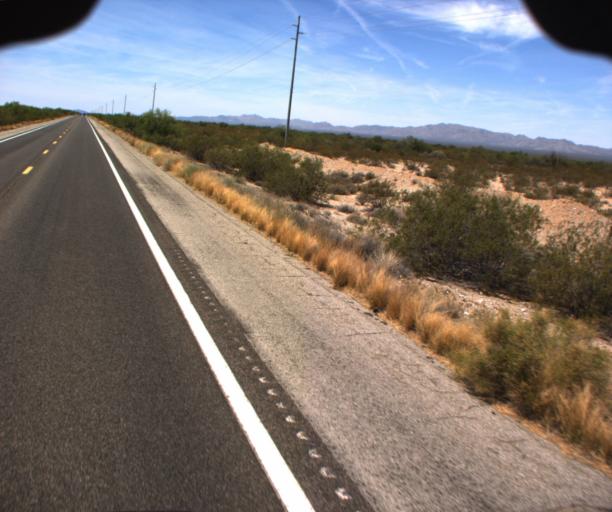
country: US
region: Arizona
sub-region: La Paz County
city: Salome
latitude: 33.8765
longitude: -113.3753
